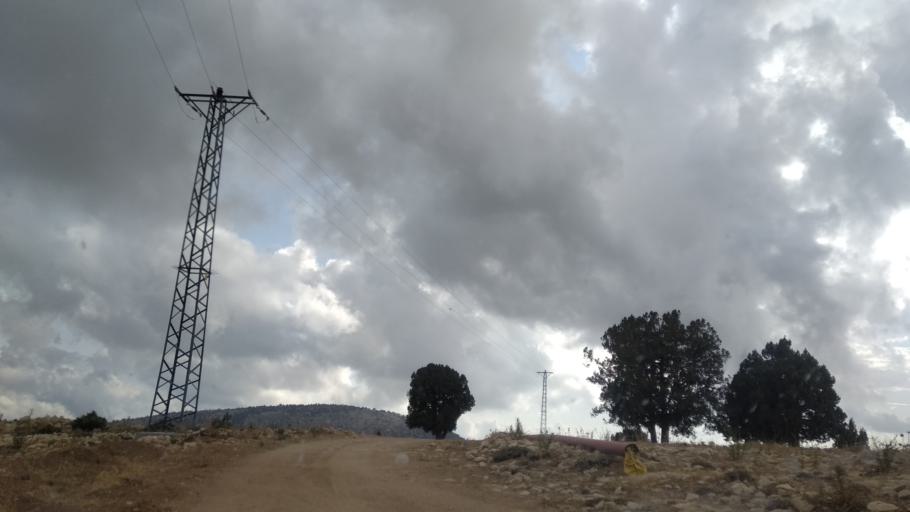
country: TR
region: Mersin
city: Sarikavak
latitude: 36.5719
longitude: 33.7491
